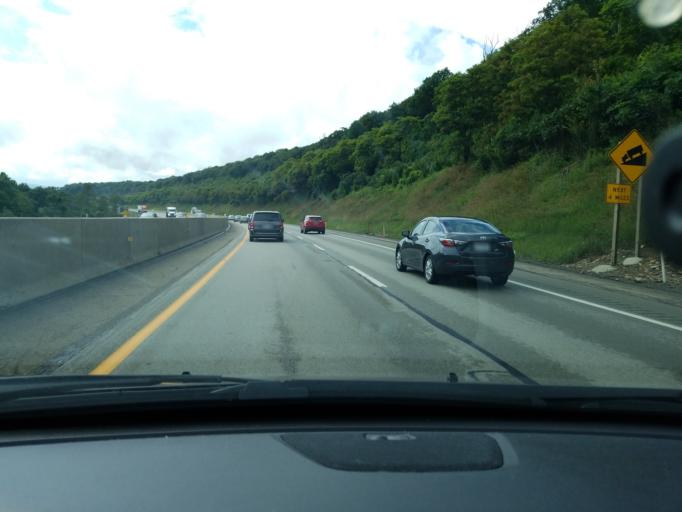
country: US
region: Pennsylvania
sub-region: Westmoreland County
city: Ligonier
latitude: 40.1165
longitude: -79.2607
